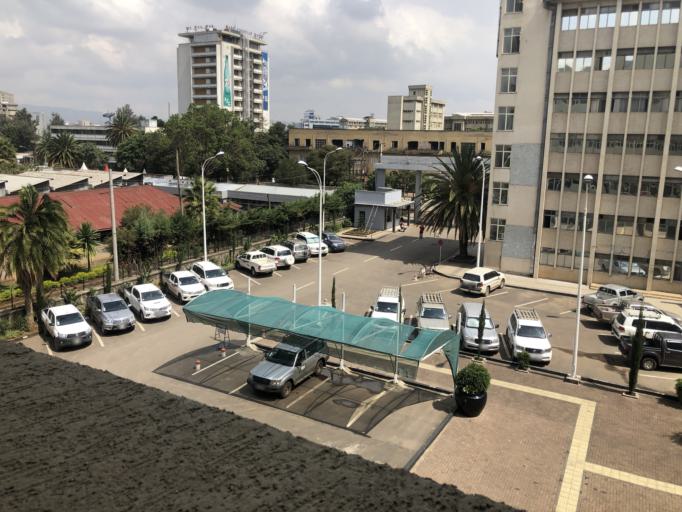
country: ET
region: Adis Abeba
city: Addis Ababa
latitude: 9.0126
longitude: 38.7481
